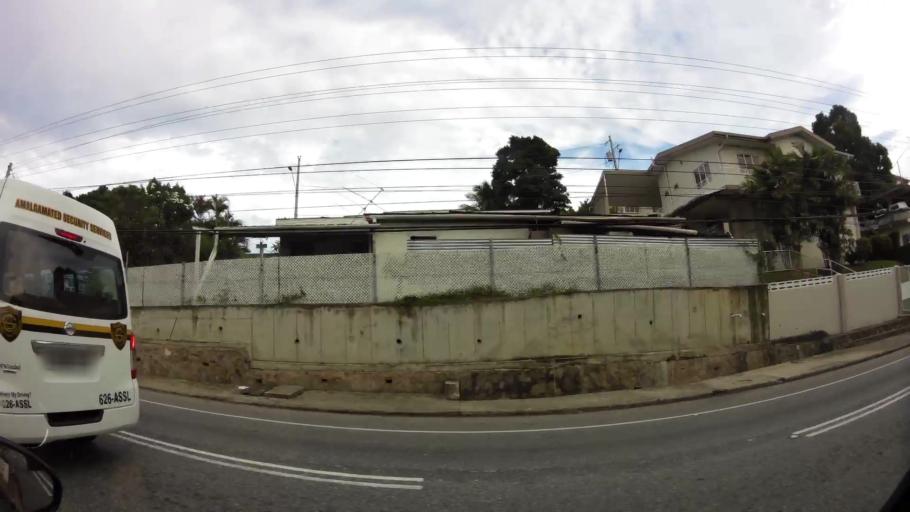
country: TT
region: Tunapuna/Piarco
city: Tunapuna
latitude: 10.6522
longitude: -61.4159
